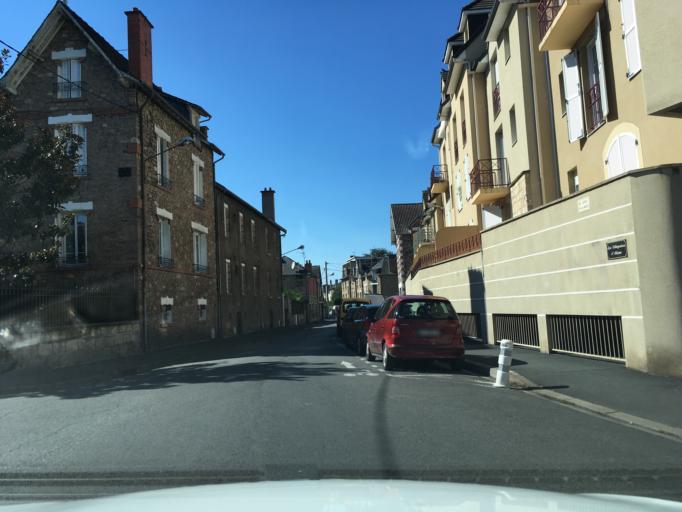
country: FR
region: Limousin
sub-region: Departement de la Correze
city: Brive-la-Gaillarde
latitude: 45.1620
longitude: 1.5293
